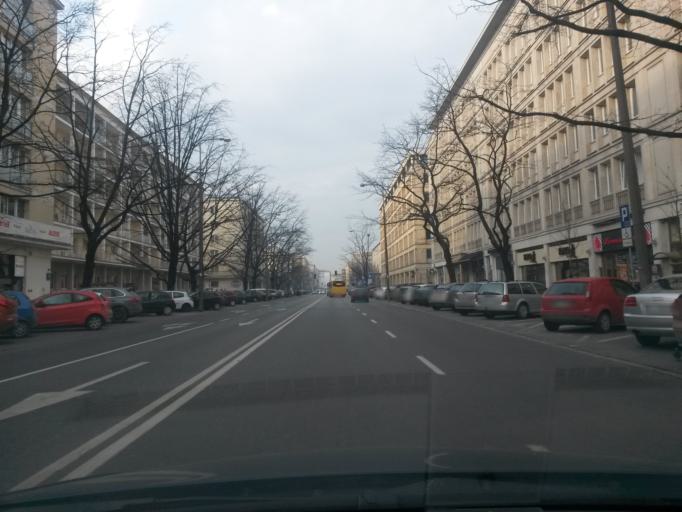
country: PL
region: Masovian Voivodeship
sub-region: Warszawa
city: Srodmiescie
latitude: 52.2257
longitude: 21.0190
